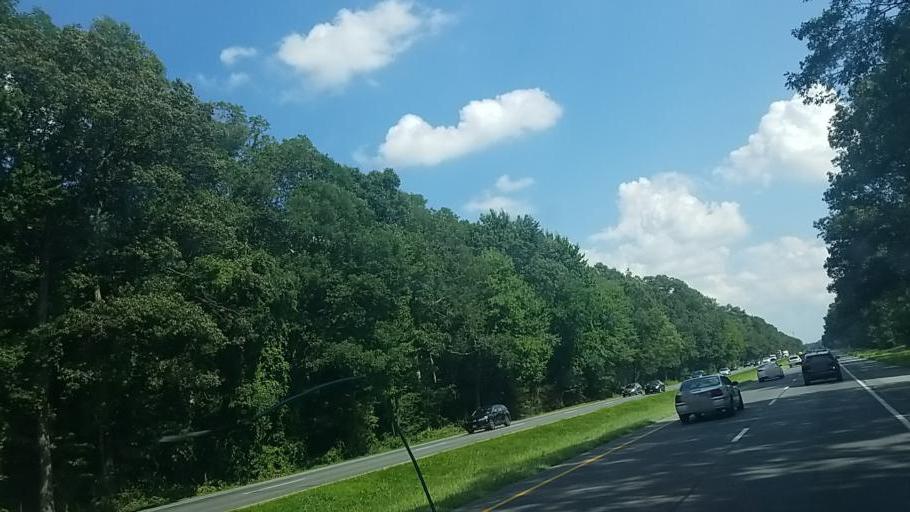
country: US
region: Delaware
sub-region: Sussex County
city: Millsboro
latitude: 38.6101
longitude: -75.3278
